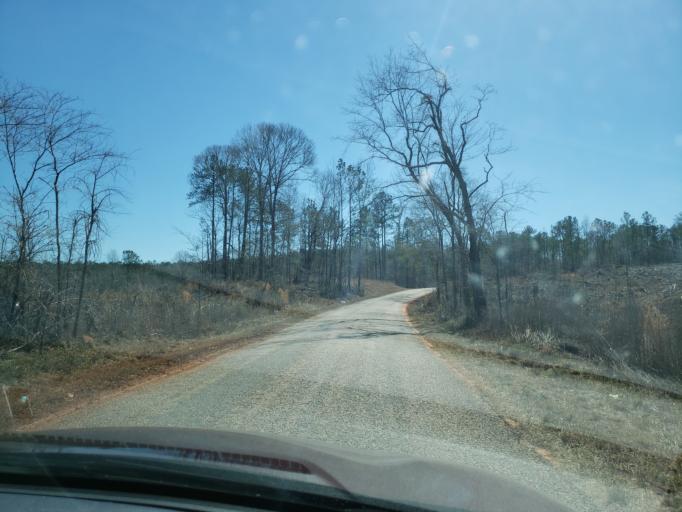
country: US
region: Alabama
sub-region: Elmore County
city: Tallassee
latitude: 32.6649
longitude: -85.8702
